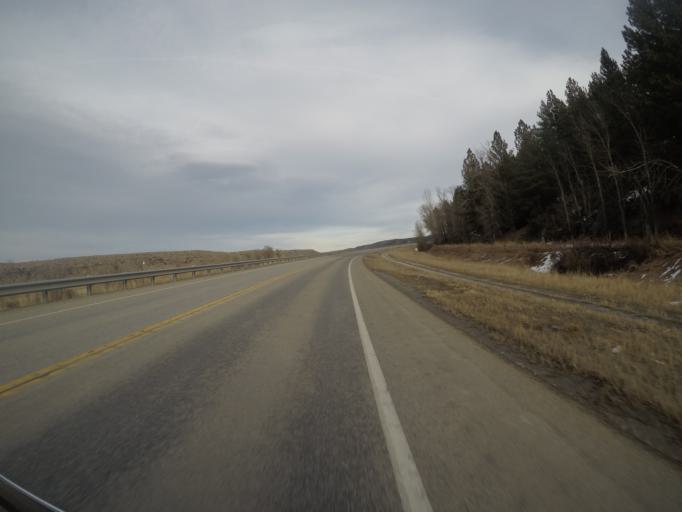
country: US
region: Montana
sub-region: Stillwater County
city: Absarokee
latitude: 45.5434
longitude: -109.4012
